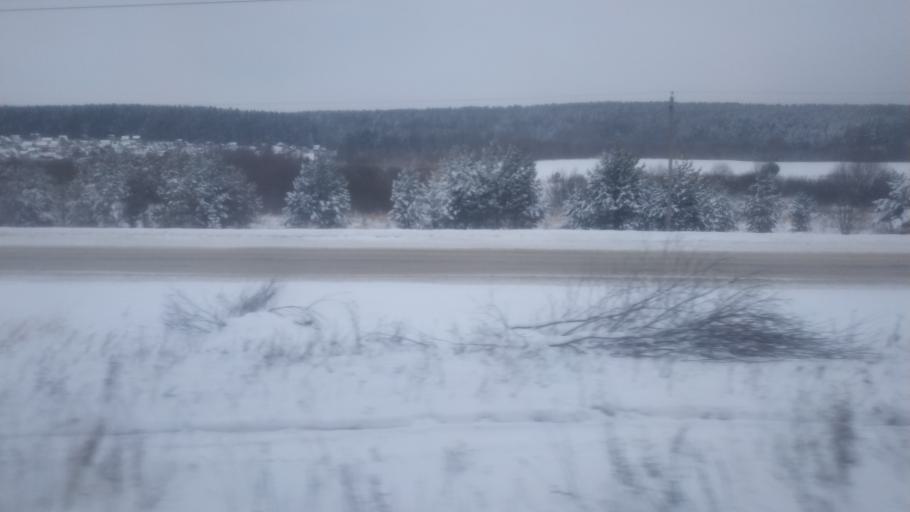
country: RU
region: Udmurtiya
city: Sigayevo
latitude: 56.4537
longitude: 53.6916
